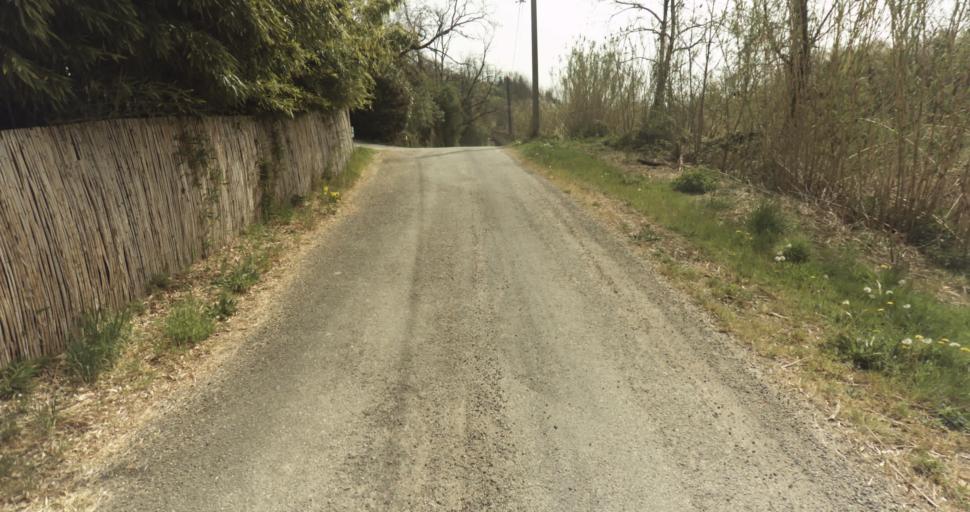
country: FR
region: Midi-Pyrenees
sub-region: Departement du Tarn-et-Garonne
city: Moissac
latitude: 44.1082
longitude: 1.0672
